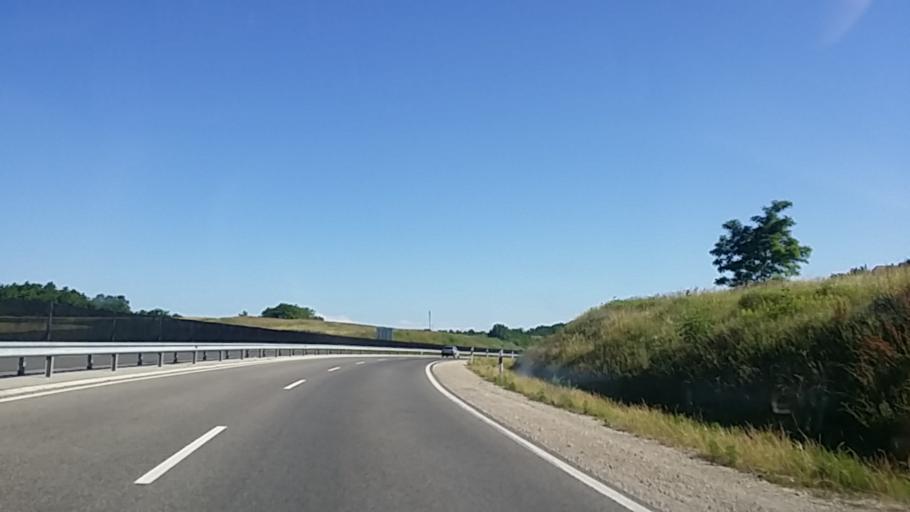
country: HU
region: Zala
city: Zalaegerszeg
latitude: 46.8360
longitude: 16.8853
